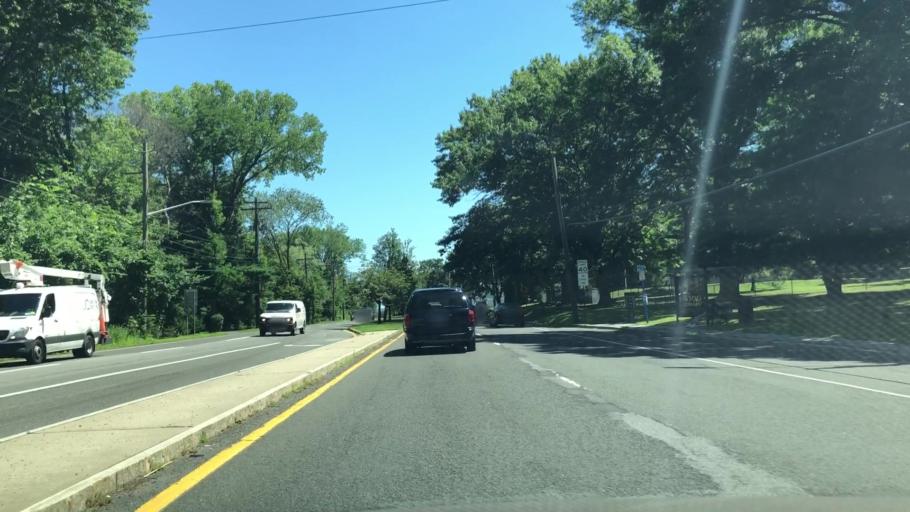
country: US
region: New York
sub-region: Westchester County
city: White Plains
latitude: 41.0056
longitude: -73.7511
